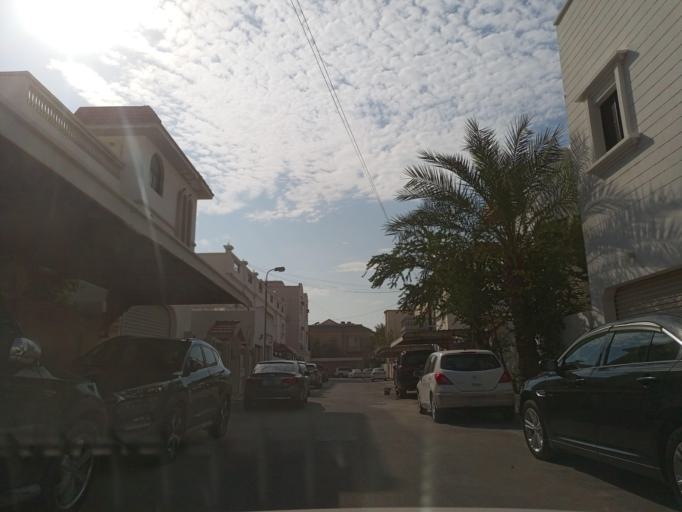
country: BH
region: Muharraq
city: Al Hadd
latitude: 26.2524
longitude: 50.6443
